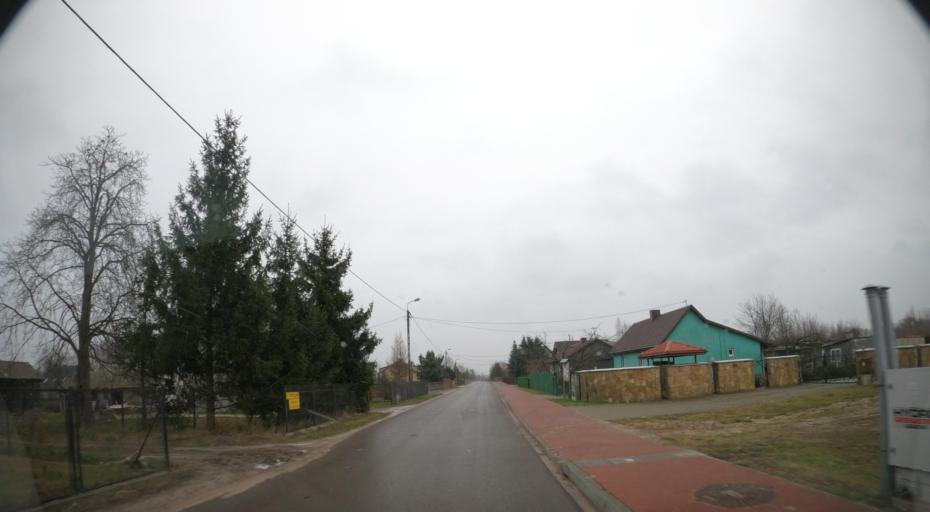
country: PL
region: Masovian Voivodeship
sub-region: Powiat radomski
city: Jedlnia-Letnisko
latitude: 51.4168
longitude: 21.2762
